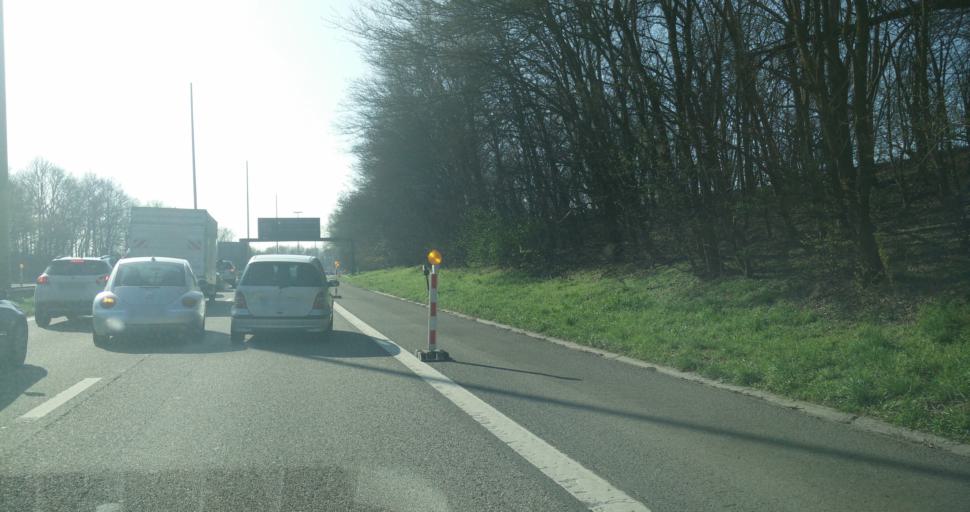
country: BE
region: Wallonia
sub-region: Province du Hainaut
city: Brunehault
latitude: 50.5094
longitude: 4.4148
